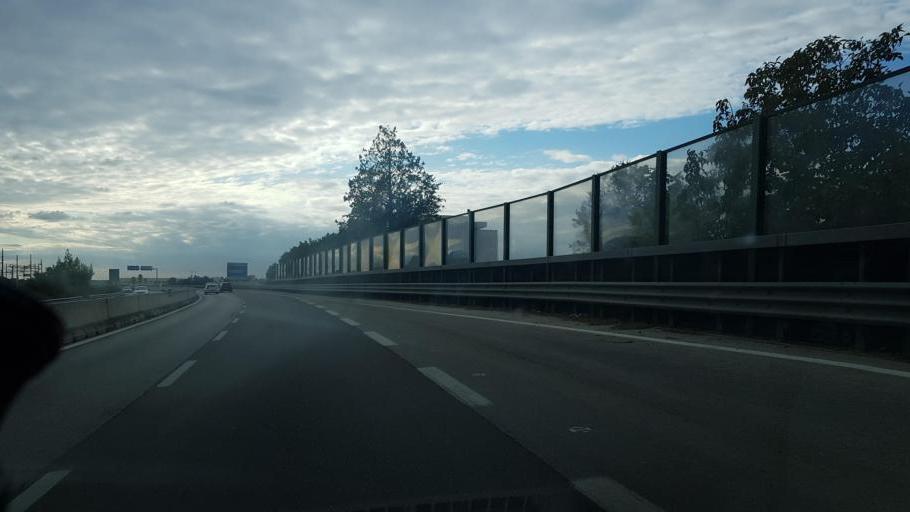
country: IT
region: Apulia
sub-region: Provincia di Brindisi
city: Latiano
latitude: 40.5586
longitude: 17.7156
